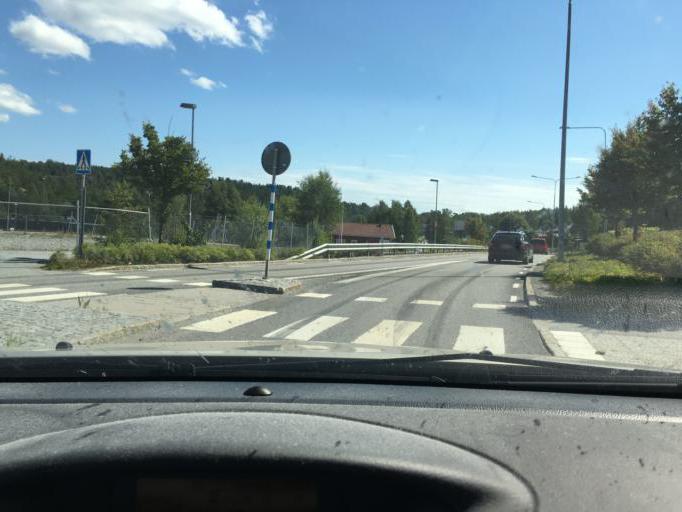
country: SE
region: Stockholm
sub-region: Varmdo Kommun
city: Mortnas
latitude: 59.2820
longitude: 18.4266
